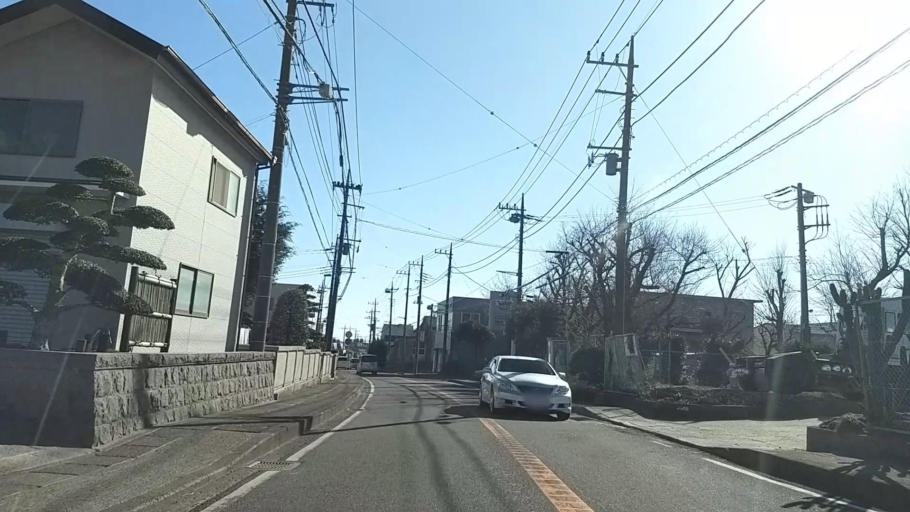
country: JP
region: Kanagawa
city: Hadano
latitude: 35.3932
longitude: 139.1992
